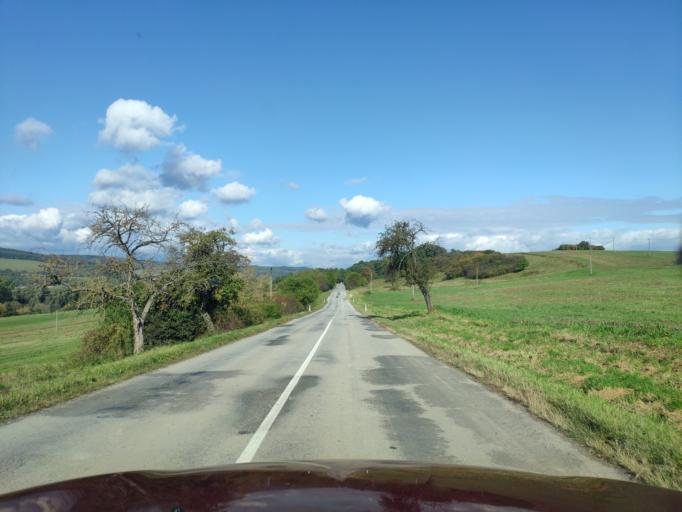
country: SK
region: Presovsky
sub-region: Okres Presov
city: Presov
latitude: 48.8801
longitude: 21.2681
